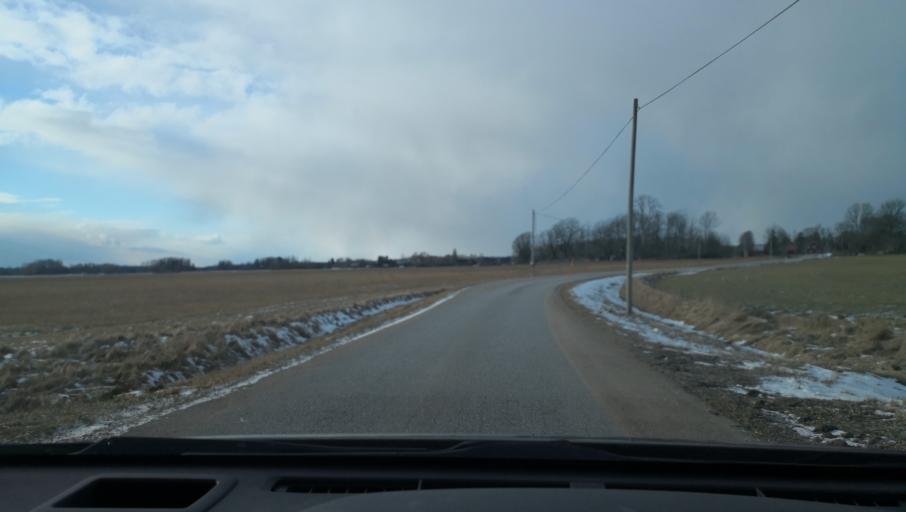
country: SE
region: Uppsala
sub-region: Enkopings Kommun
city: Irsta
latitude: 59.6976
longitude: 16.9447
